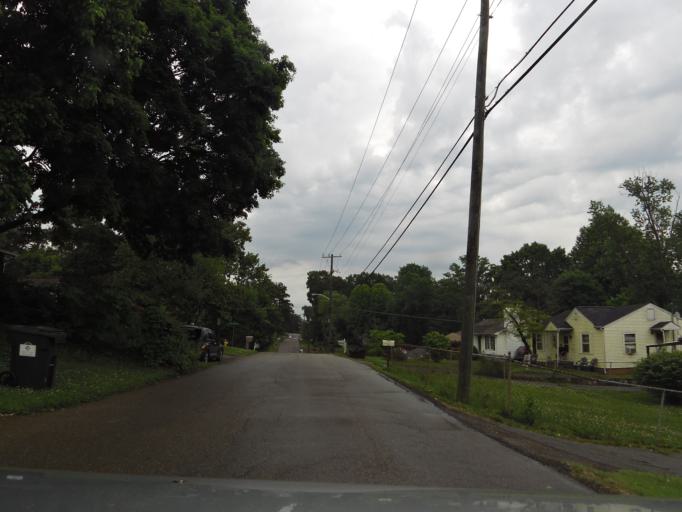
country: US
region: Tennessee
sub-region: Knox County
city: Knoxville
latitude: 35.9996
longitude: -83.9009
